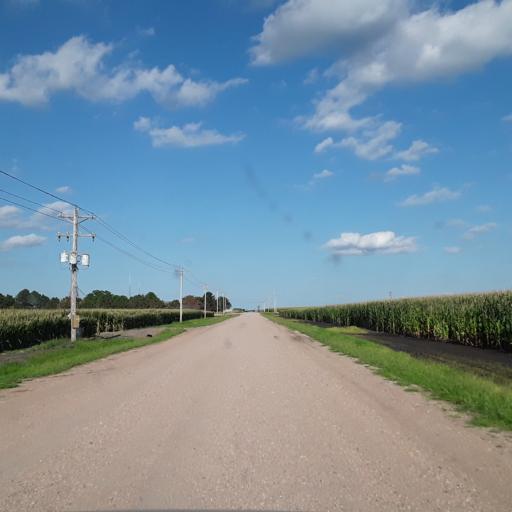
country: US
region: Nebraska
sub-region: Hall County
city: Wood River
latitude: 40.9168
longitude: -98.5927
